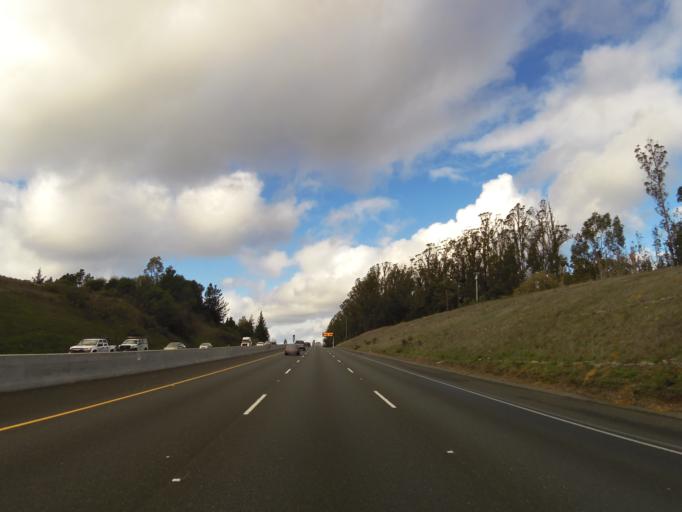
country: US
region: California
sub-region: Sonoma County
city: Cotati
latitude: 38.3060
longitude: -122.7101
